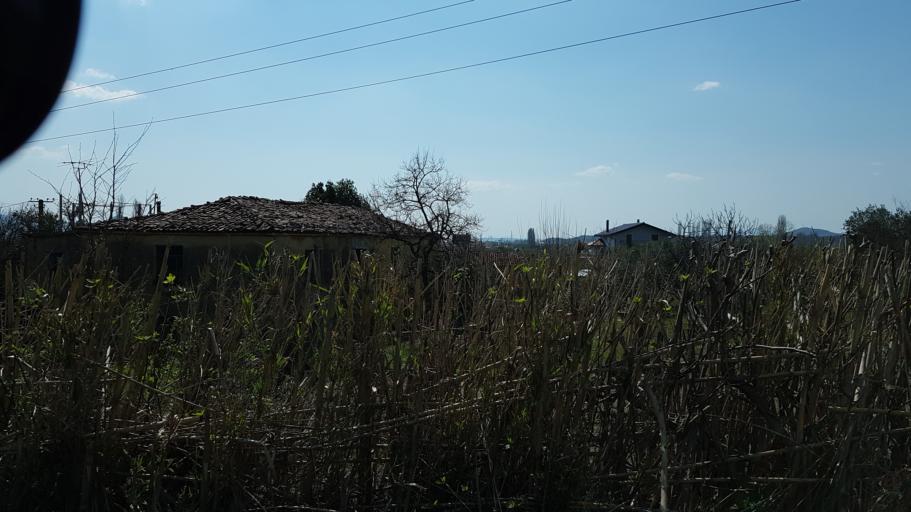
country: AL
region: Shkoder
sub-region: Rrethi i Shkodres
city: Guri i Zi
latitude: 42.0219
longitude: 19.5768
